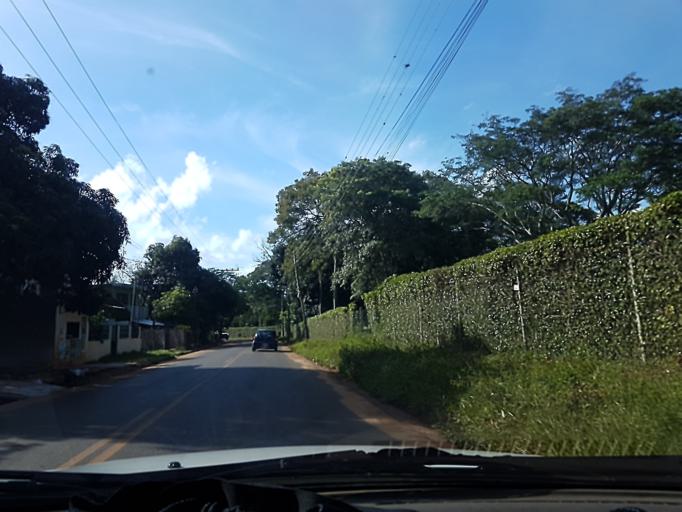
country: PY
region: Central
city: Limpio
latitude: -25.1921
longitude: -57.4620
